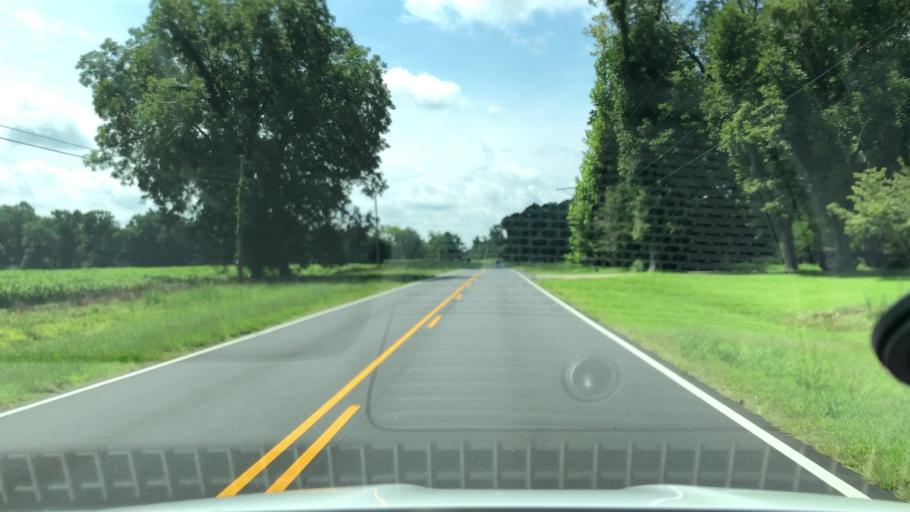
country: US
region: North Carolina
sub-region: Martin County
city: Williamston
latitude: 35.7616
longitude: -77.0748
